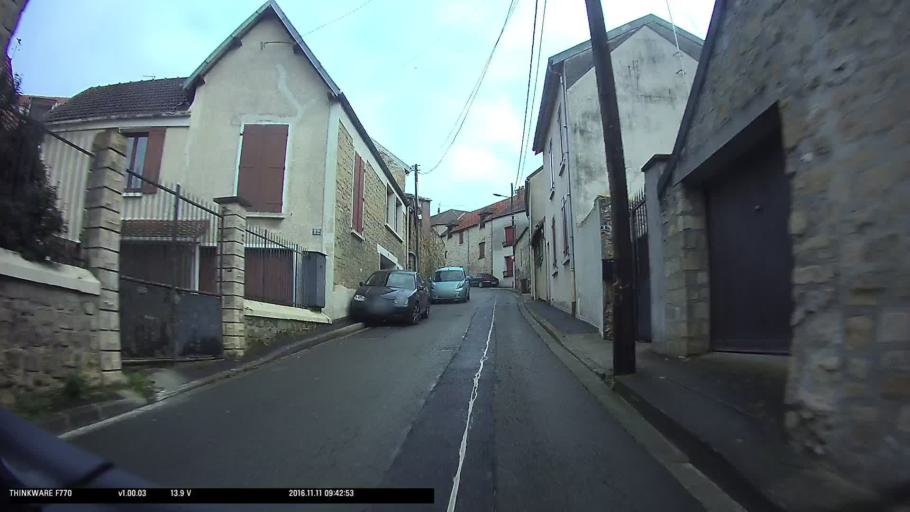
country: FR
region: Ile-de-France
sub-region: Departement du Val-d'Oise
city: Osny
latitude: 49.0678
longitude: 2.0517
